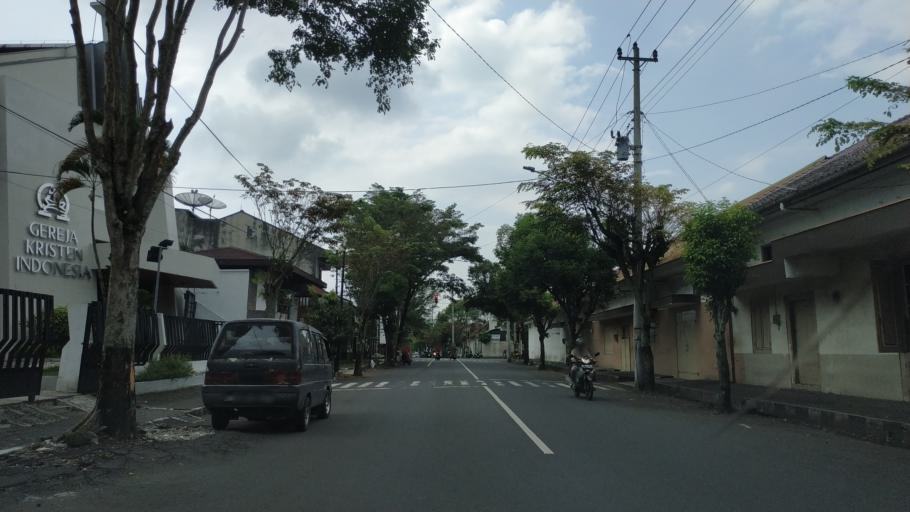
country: ID
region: Central Java
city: Magelang
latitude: -7.3143
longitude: 110.1772
